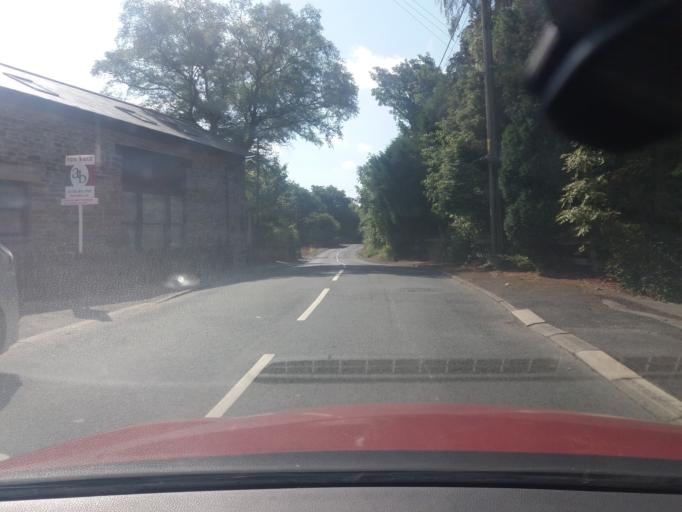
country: GB
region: England
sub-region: Lancashire
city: Adlington
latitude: 53.6252
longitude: -2.6159
